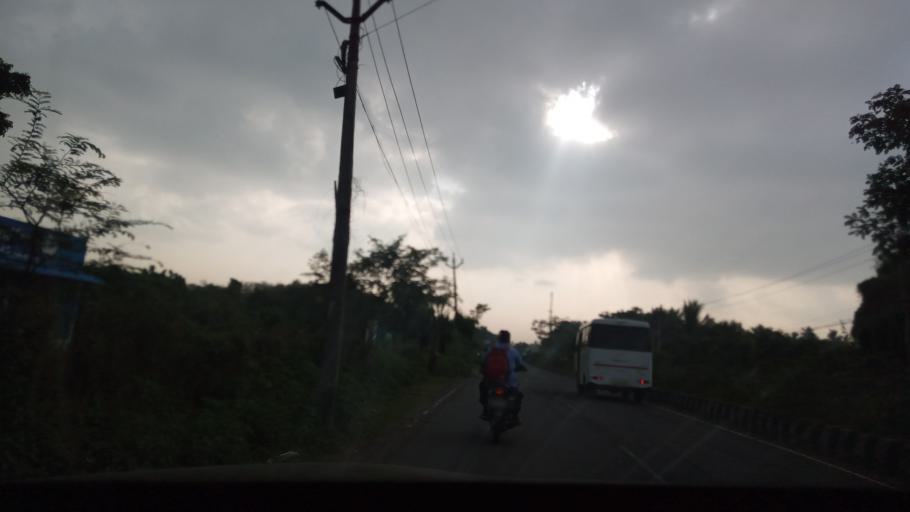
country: IN
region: Tamil Nadu
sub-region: Kancheepuram
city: Vengavasal
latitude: 12.7960
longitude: 80.2056
